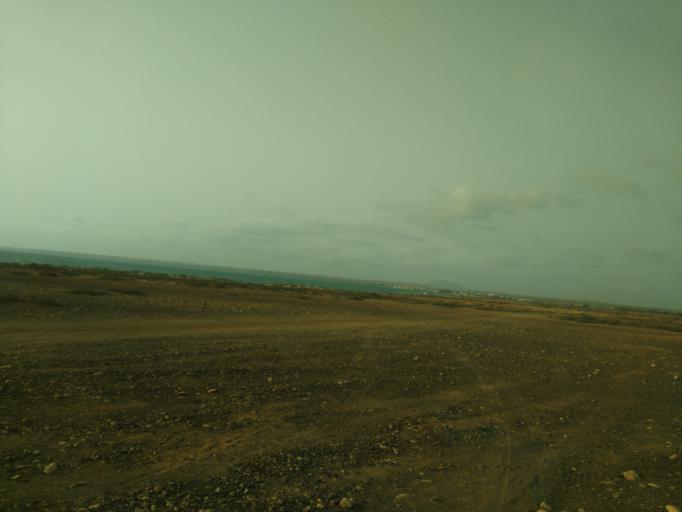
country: CV
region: Sal
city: Santa Maria
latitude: 16.6589
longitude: -22.9393
